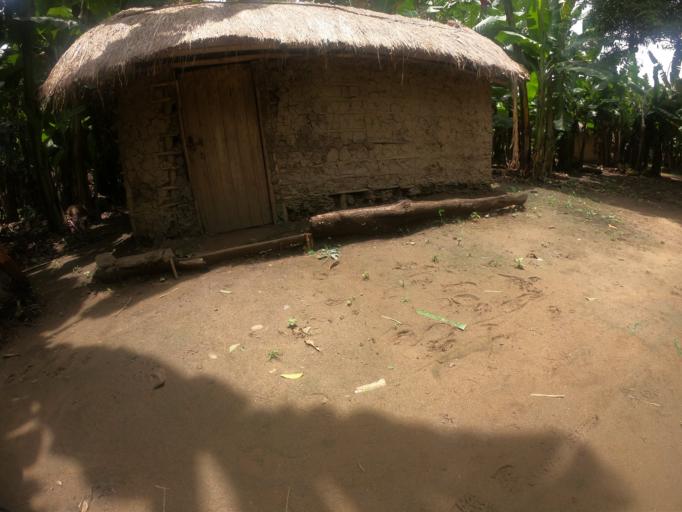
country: TZ
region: Mbeya
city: Kyela
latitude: -9.6429
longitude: 33.8155
